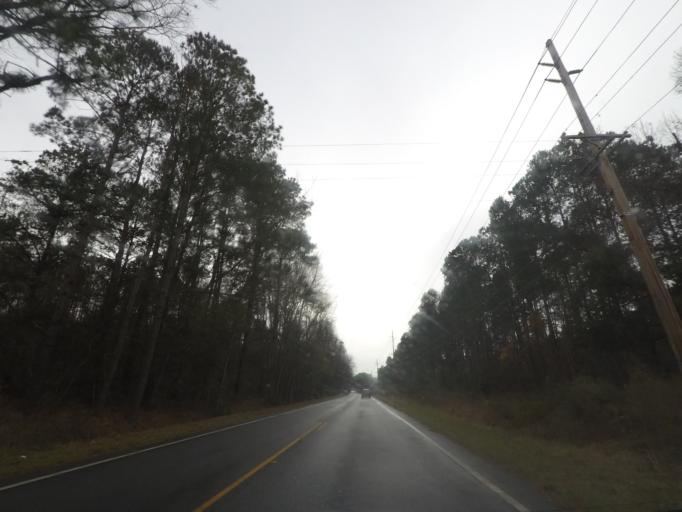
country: US
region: South Carolina
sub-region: Charleston County
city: Meggett
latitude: 32.6584
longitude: -80.3414
